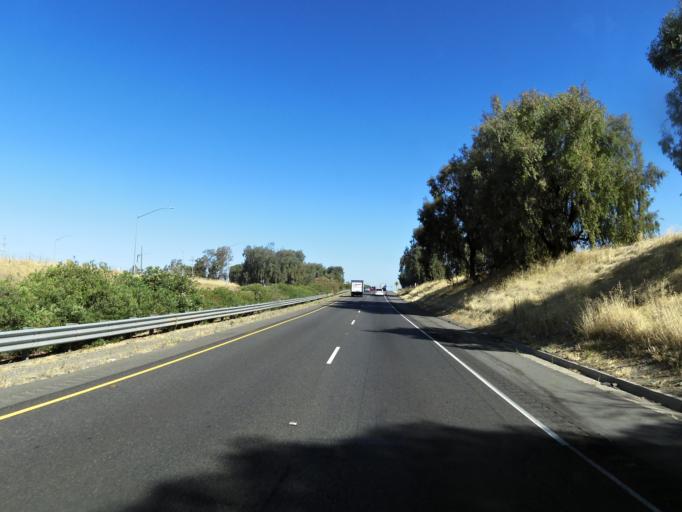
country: US
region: California
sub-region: Sacramento County
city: Galt
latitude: 38.2912
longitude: -121.3122
